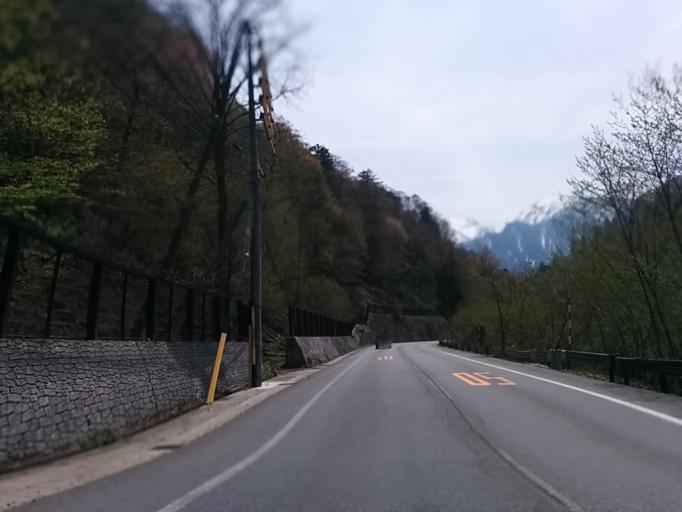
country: JP
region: Gifu
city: Takayama
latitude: 36.2035
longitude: 137.5519
